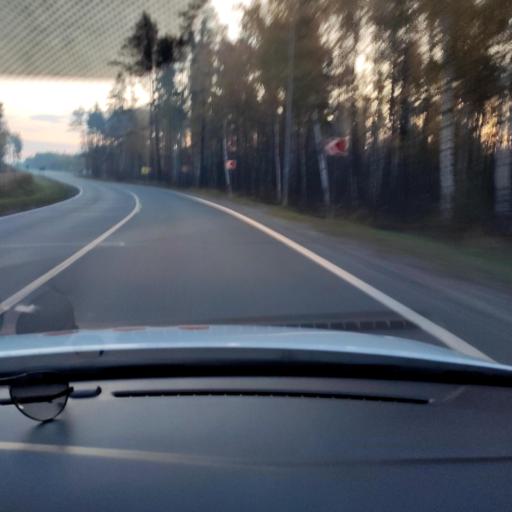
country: RU
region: Tatarstan
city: Stolbishchi
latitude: 55.6333
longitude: 49.1010
